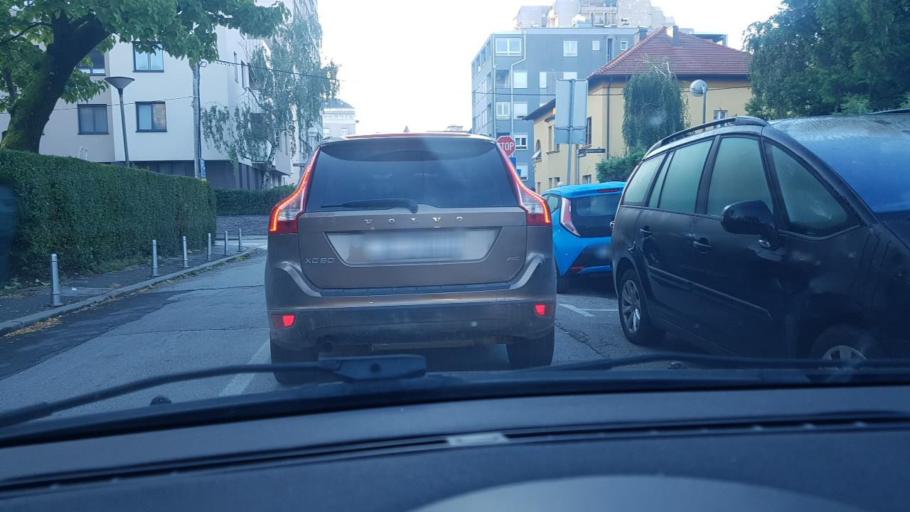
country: HR
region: Grad Zagreb
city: Zagreb
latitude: 45.8189
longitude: 16.0080
